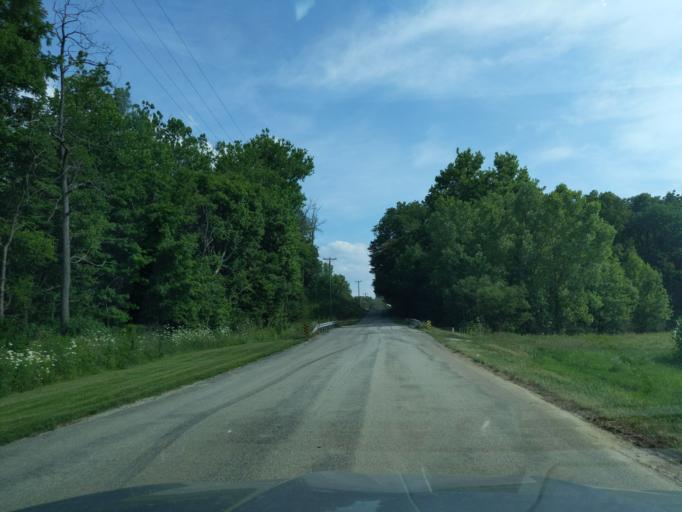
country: US
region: Indiana
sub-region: Decatur County
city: Greensburg
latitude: 39.2967
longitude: -85.4701
